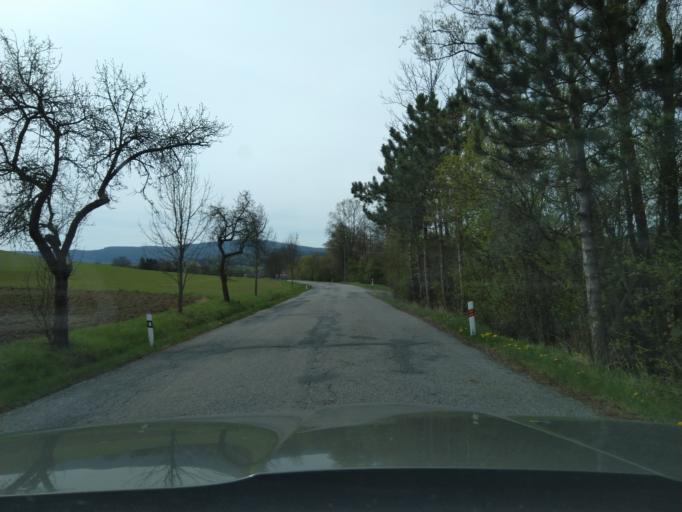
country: CZ
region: Plzensky
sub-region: Okres Klatovy
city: Kasperske Hory
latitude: 49.2113
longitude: 13.6131
